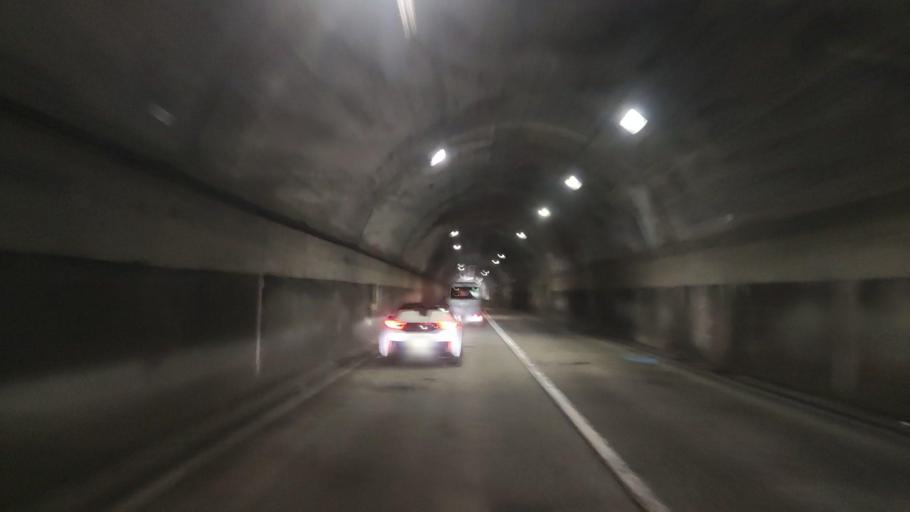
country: JP
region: Mie
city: Owase
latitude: 34.1700
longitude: 136.2897
